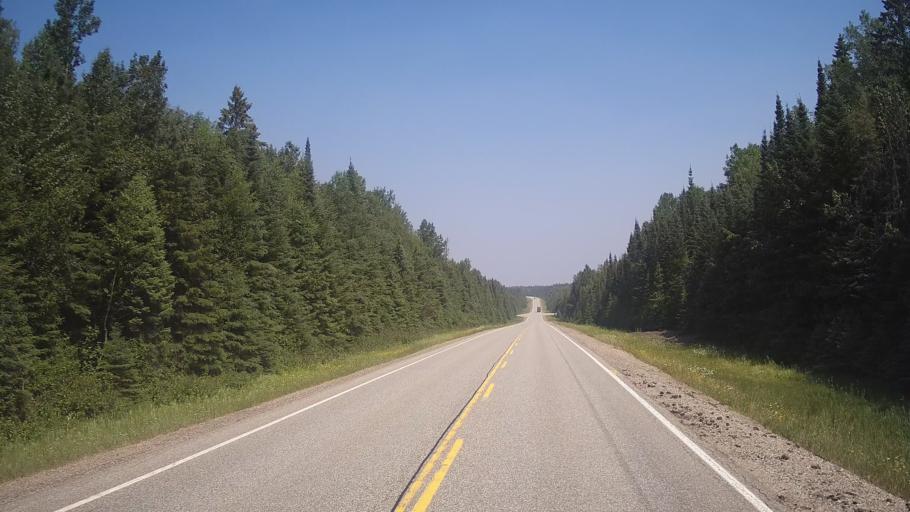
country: CA
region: Ontario
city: Timmins
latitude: 48.0889
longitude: -81.5949
